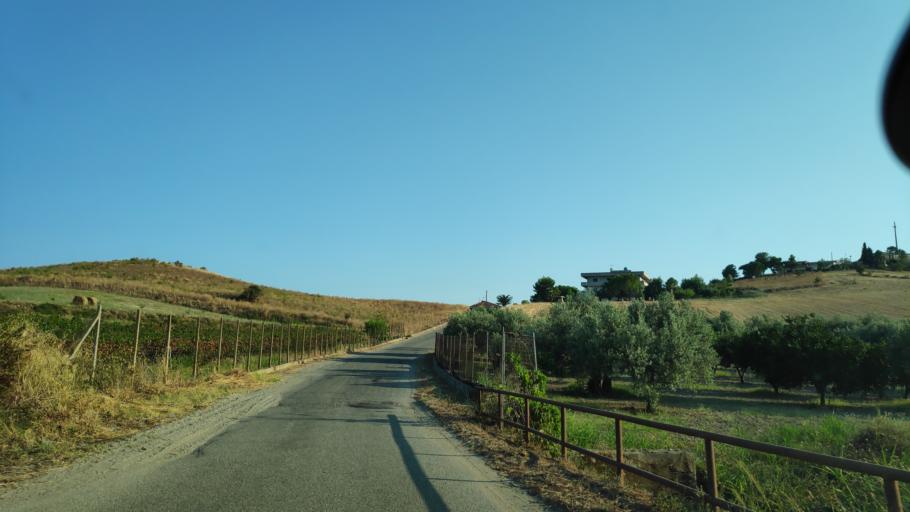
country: IT
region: Calabria
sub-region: Provincia di Reggio Calabria
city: Monasterace Marina
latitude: 38.4419
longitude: 16.5716
